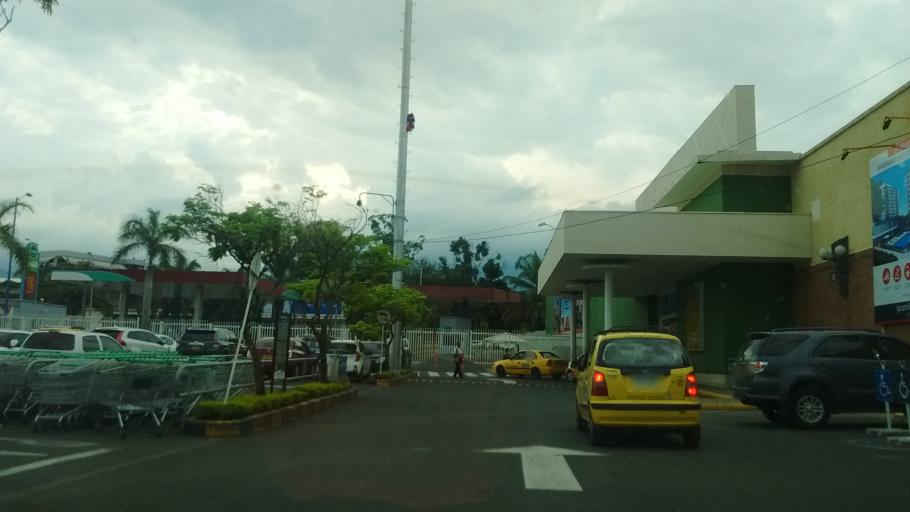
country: CO
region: Valle del Cauca
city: Cali
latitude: 3.3689
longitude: -76.5286
